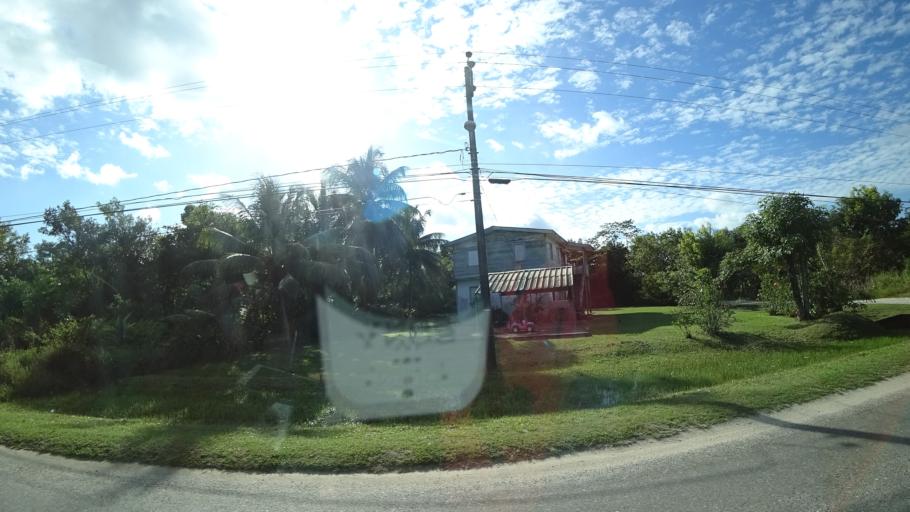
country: BZ
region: Belize
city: Belize City
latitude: 17.5646
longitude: -88.4062
